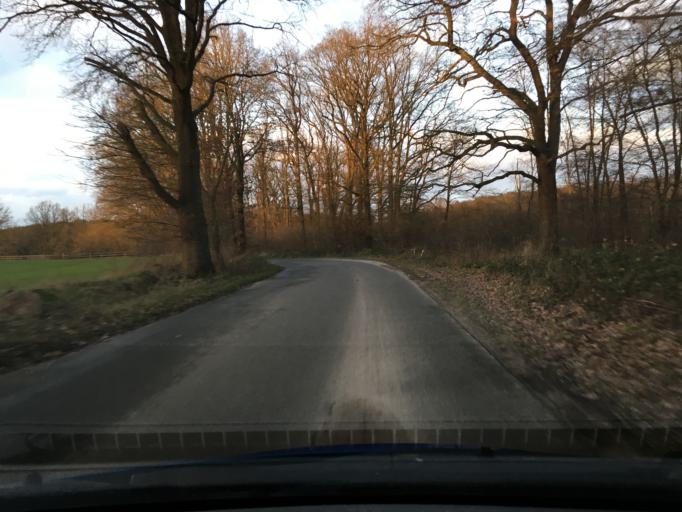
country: DE
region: Lower Saxony
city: Amelinghausen
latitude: 53.1392
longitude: 10.2037
